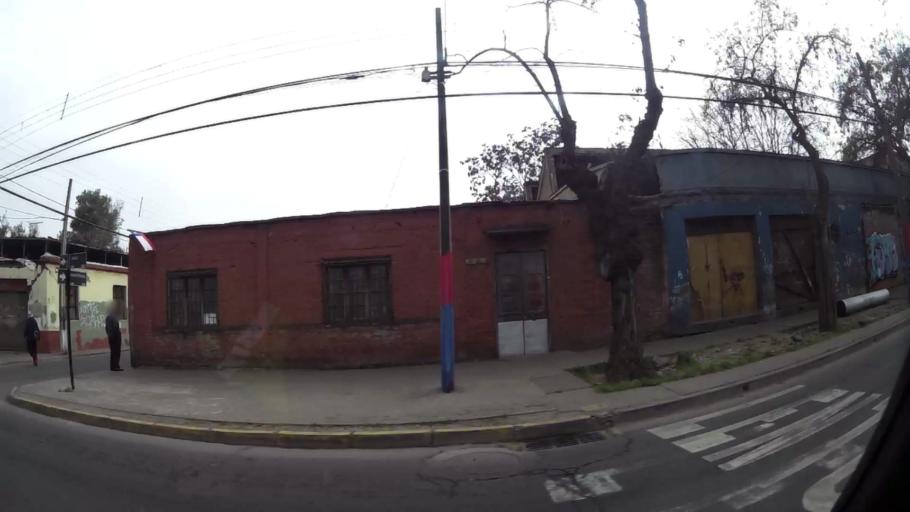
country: CL
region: Santiago Metropolitan
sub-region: Provincia de Santiago
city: Santiago
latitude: -33.4700
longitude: -70.6509
